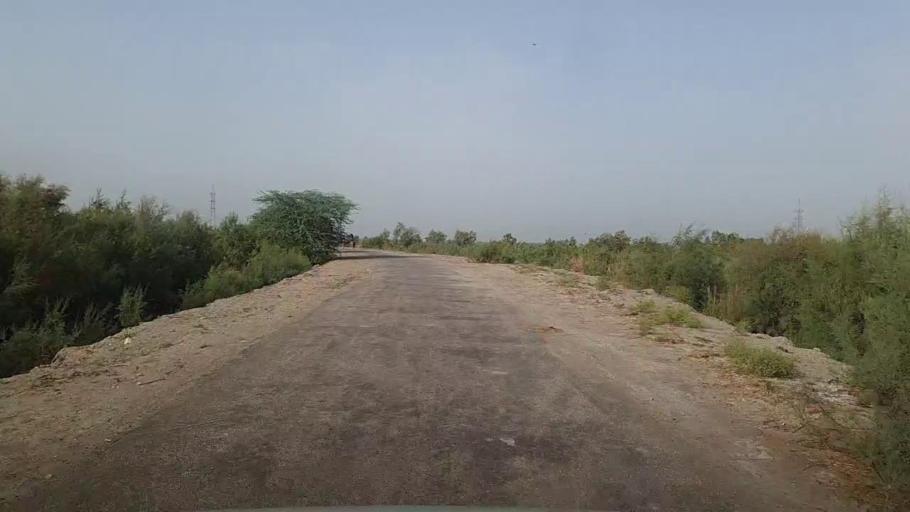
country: PK
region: Sindh
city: Khairpur Nathan Shah
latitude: 27.0854
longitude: 67.7924
